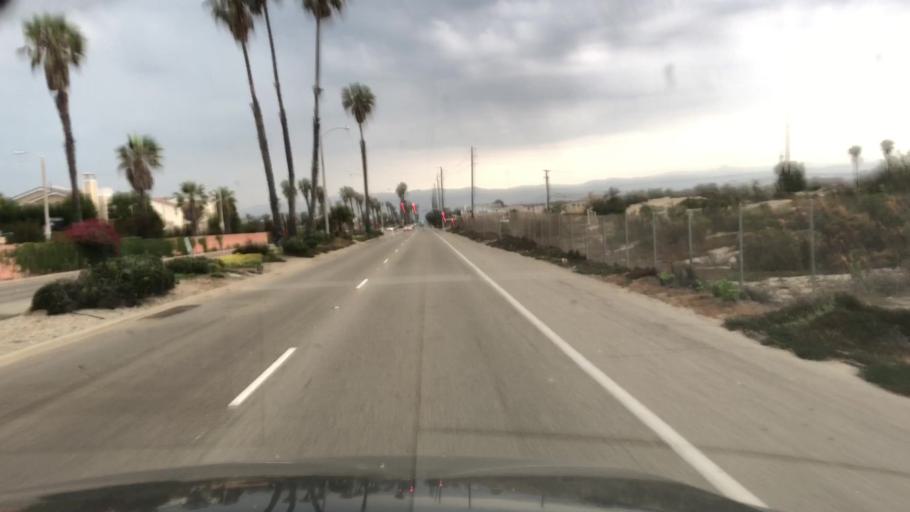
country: US
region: California
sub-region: Ventura County
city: Oxnard Shores
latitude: 34.1888
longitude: -119.2375
